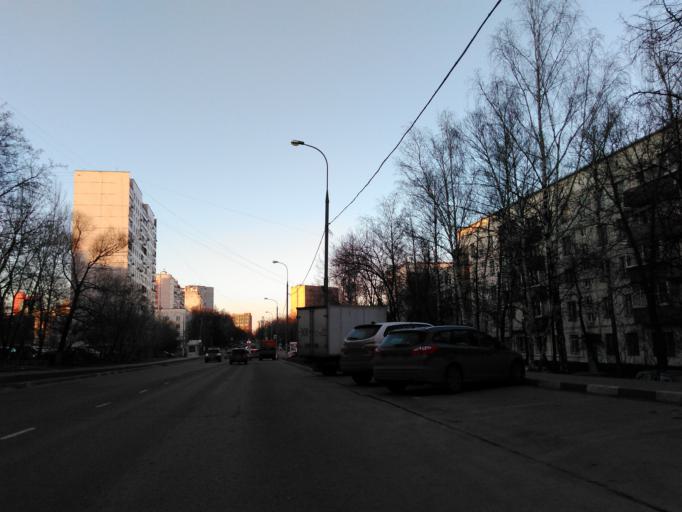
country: RU
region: Moskovskaya
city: Cheremushki
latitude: 55.6409
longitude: 37.5397
